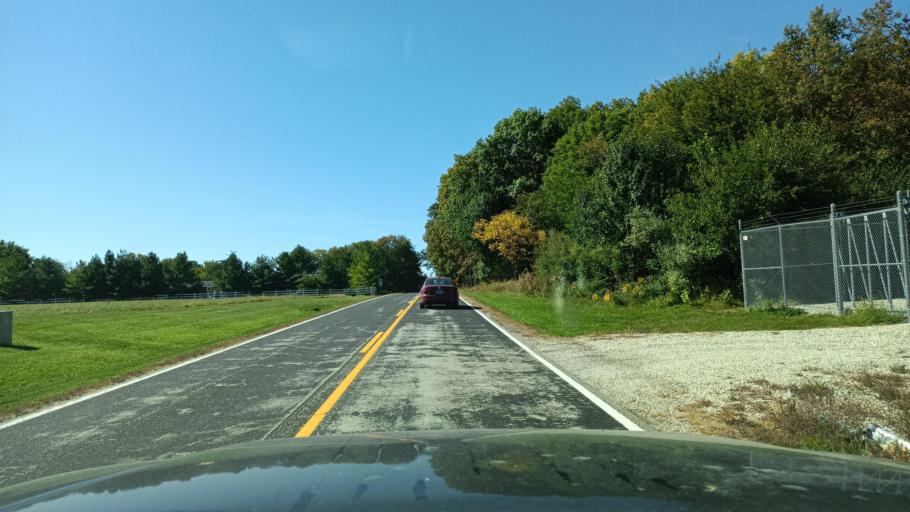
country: US
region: Illinois
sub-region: Champaign County
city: Lake of the Woods
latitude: 40.2077
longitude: -88.3667
